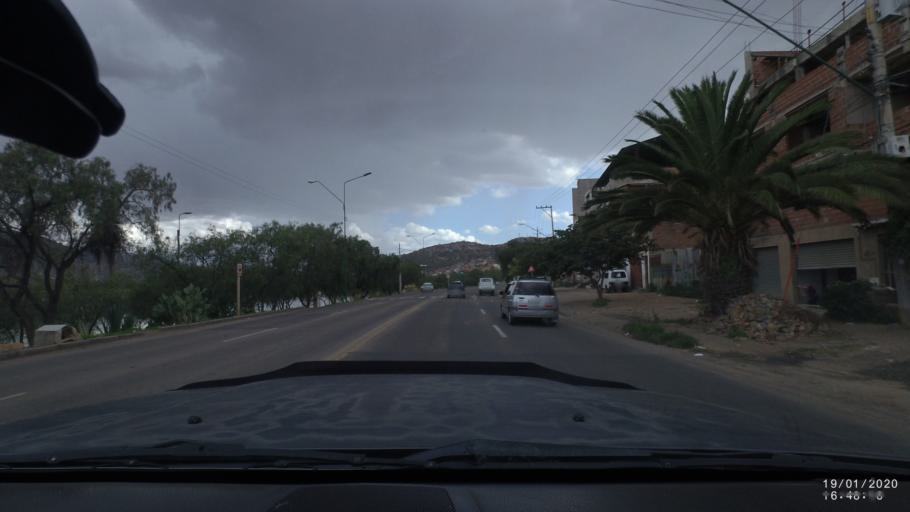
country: BO
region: Cochabamba
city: Cochabamba
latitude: -17.4097
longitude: -66.1427
